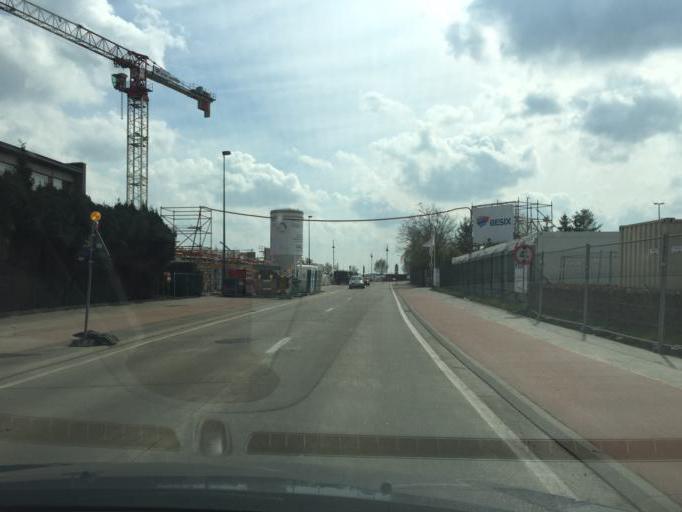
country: BE
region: Flanders
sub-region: Provincie Oost-Vlaanderen
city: Aalter
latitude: 51.0846
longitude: 3.4442
